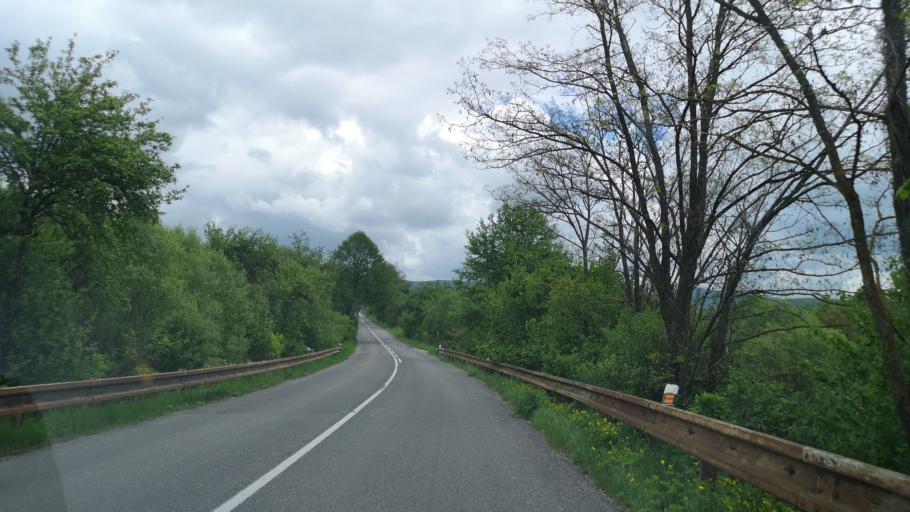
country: SK
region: Kosicky
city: Dobsina
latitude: 48.6356
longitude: 20.3352
